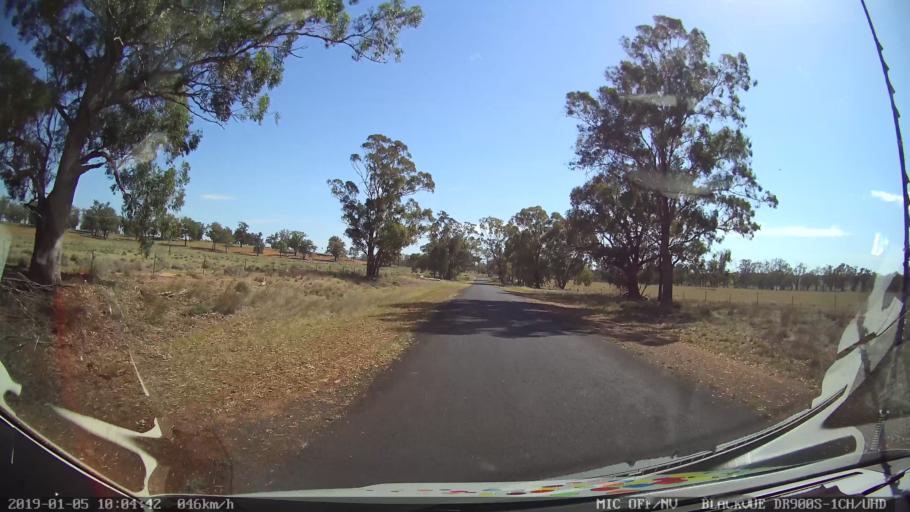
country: AU
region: New South Wales
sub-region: Gilgandra
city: Gilgandra
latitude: -31.6723
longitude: 148.8615
